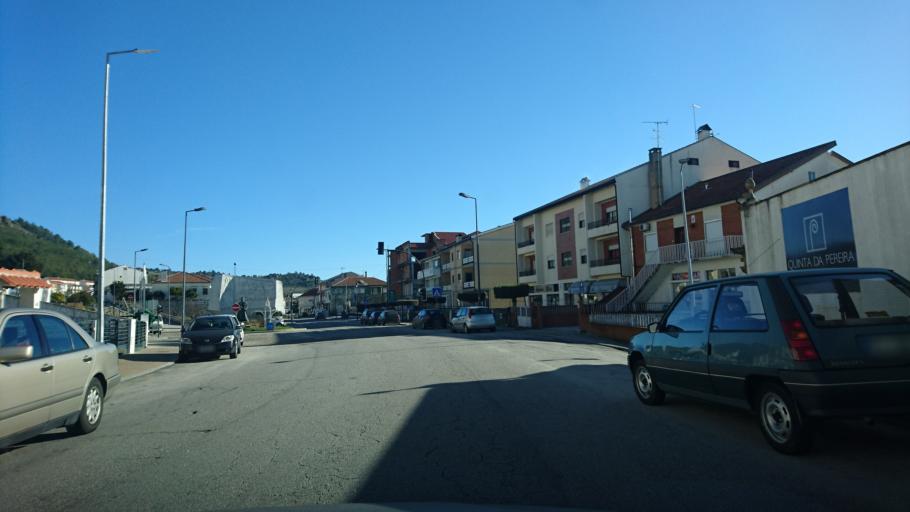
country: PT
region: Braganca
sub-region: Braganca Municipality
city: Vila Flor
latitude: 41.3081
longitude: -7.1597
